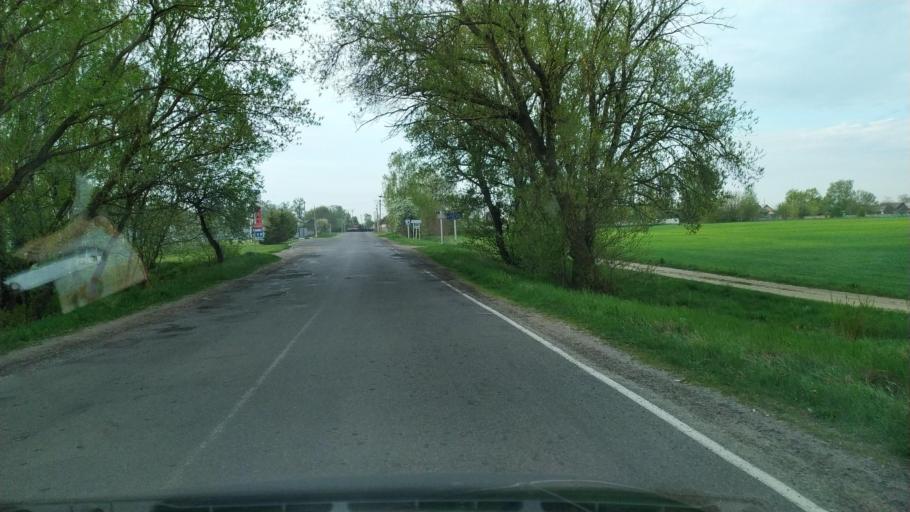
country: BY
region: Brest
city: Zhabinka
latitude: 52.1597
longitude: 24.0856
